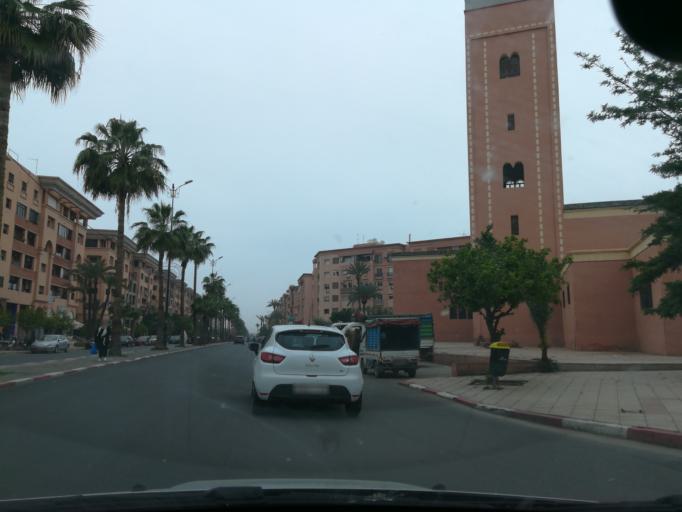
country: MA
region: Marrakech-Tensift-Al Haouz
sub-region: Marrakech
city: Marrakesh
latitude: 31.6565
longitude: -8.0040
